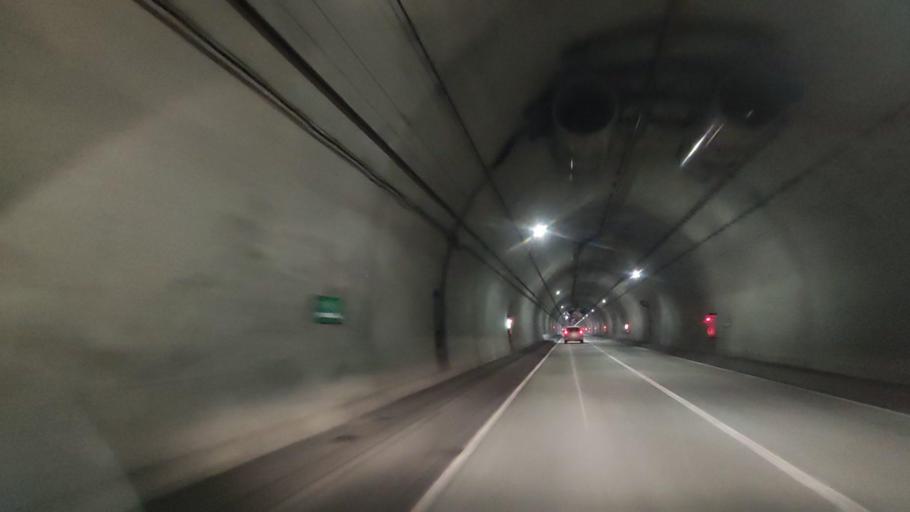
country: JP
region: Hokkaido
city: Rumoi
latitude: 43.7222
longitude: 141.3303
